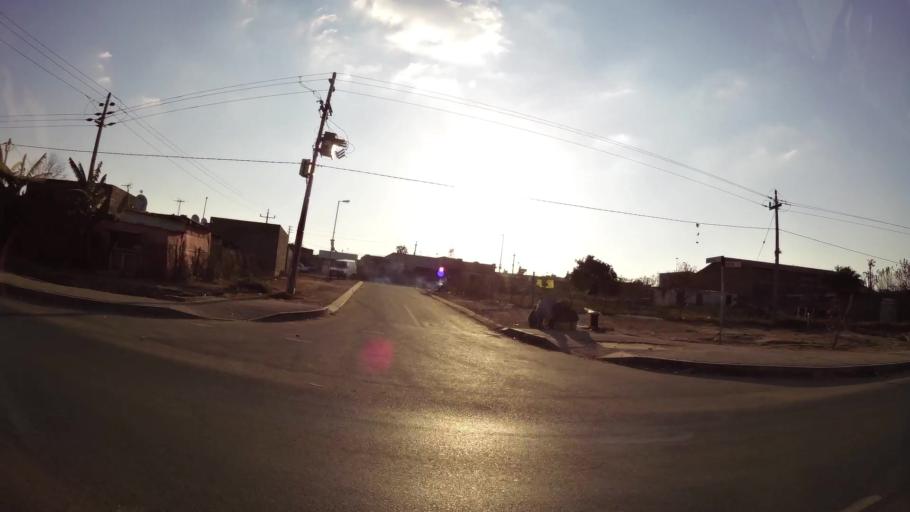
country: ZA
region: Gauteng
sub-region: Ekurhuleni Metropolitan Municipality
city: Tembisa
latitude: -26.0125
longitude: 28.1863
